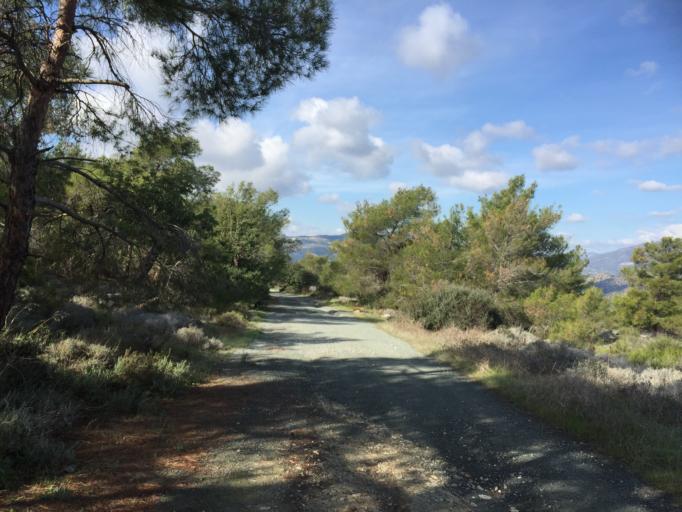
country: CY
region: Larnaka
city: Agios Tychon
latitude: 34.7487
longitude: 33.1234
